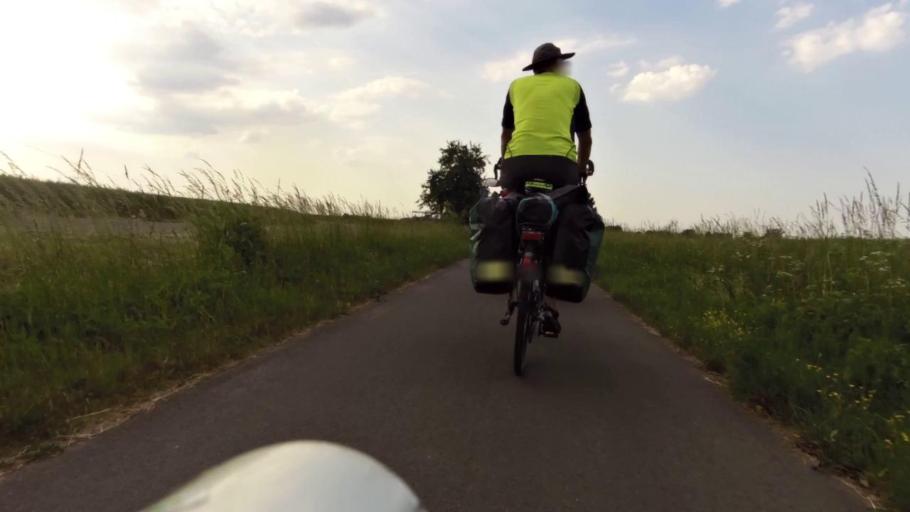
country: PL
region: Kujawsko-Pomorskie
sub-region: Powiat torunski
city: Lubianka
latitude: 53.1253
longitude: 18.4674
